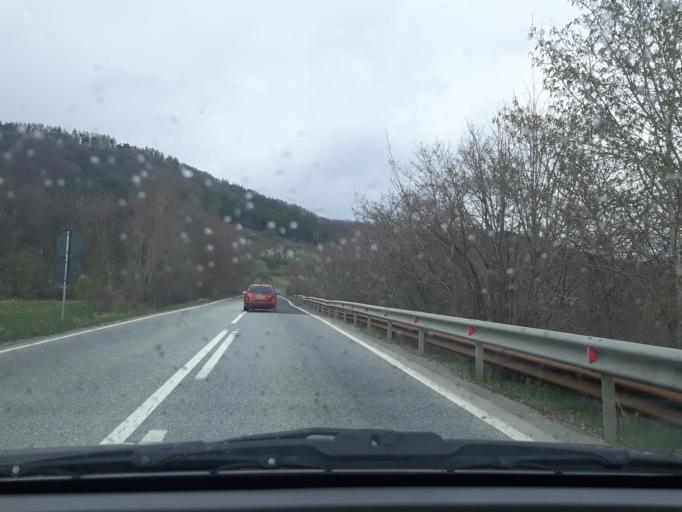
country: RO
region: Harghita
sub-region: Comuna Lupeni
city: Lupeni
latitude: 46.4086
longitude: 25.2180
